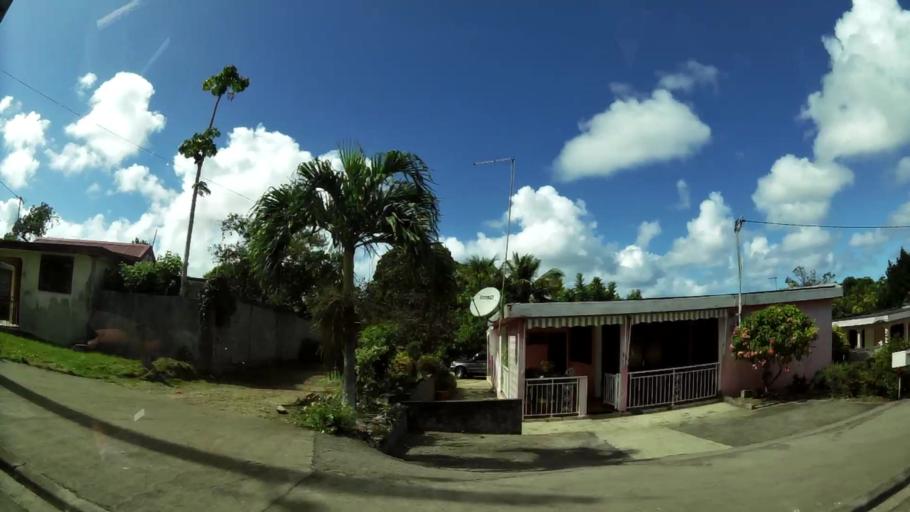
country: GP
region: Guadeloupe
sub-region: Guadeloupe
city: Anse-Bertrand
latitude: 16.4398
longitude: -61.4749
